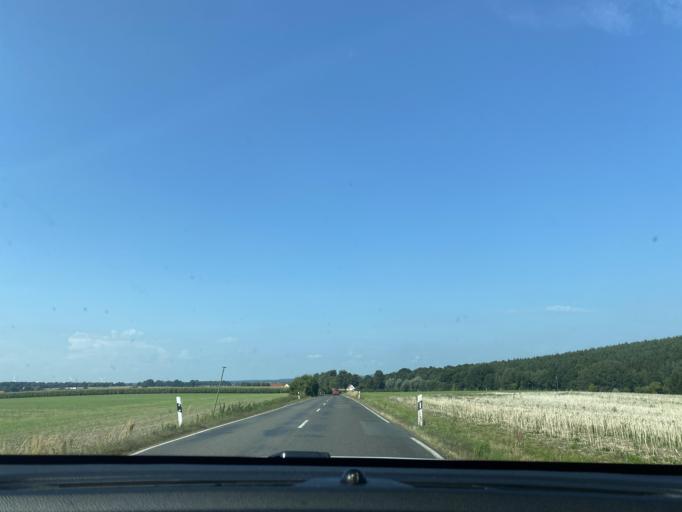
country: DE
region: Saxony
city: Reichenbach
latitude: 51.1644
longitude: 14.7875
